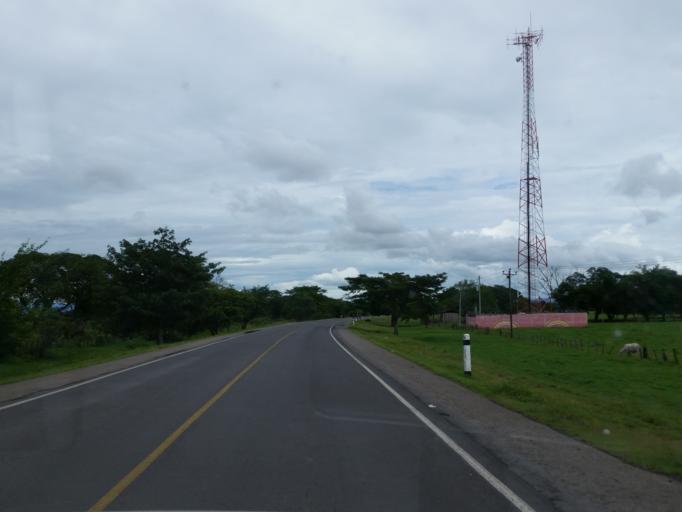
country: NI
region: Chinandega
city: Somotillo
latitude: 12.8314
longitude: -86.8956
